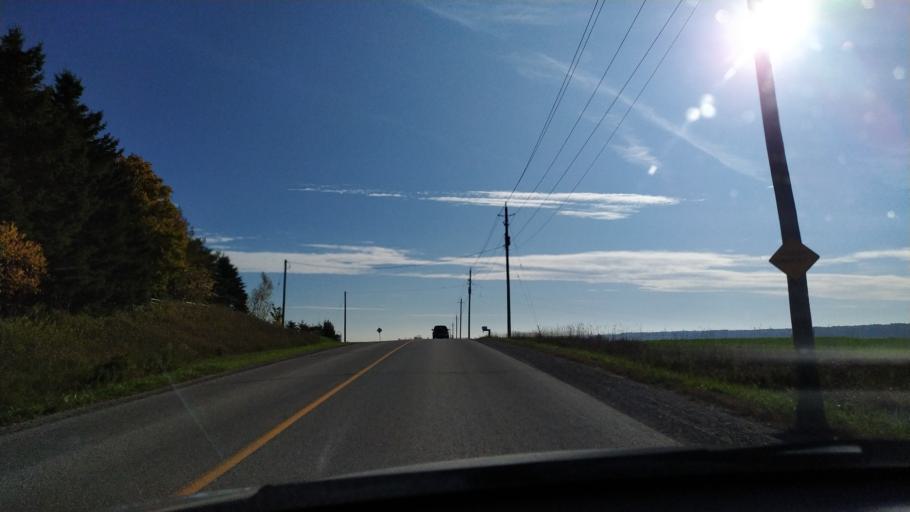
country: CA
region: Ontario
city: Waterloo
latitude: 43.4946
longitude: -80.7479
